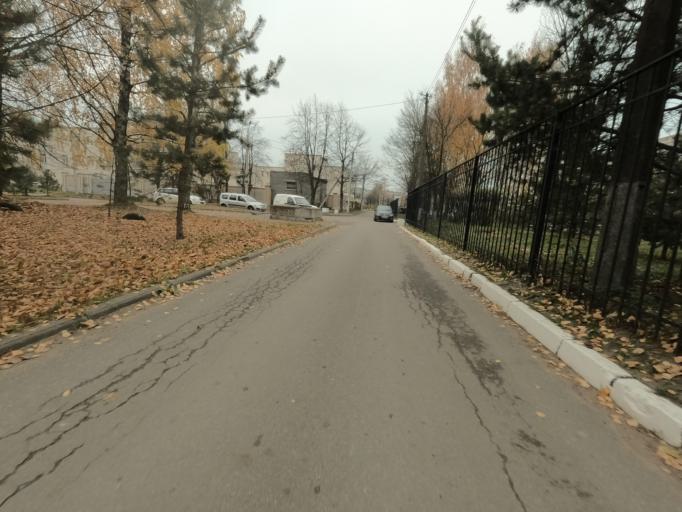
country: RU
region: Leningrad
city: Kirovsk
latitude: 59.8801
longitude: 30.9999
